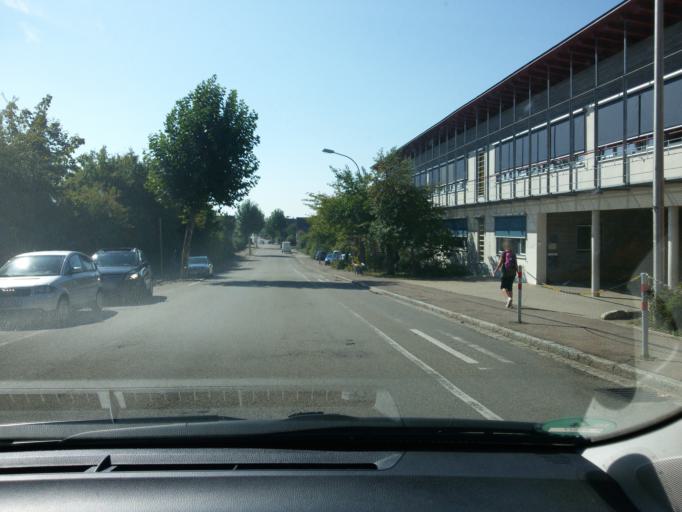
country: DE
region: Bavaria
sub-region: Swabia
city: Oettingen in Bayern
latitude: 48.9531
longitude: 10.5982
